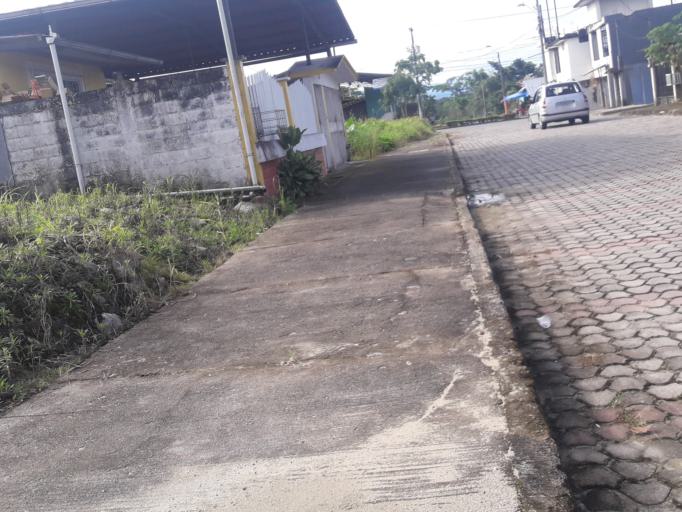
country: EC
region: Napo
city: Tena
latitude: -0.9841
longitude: -77.8110
